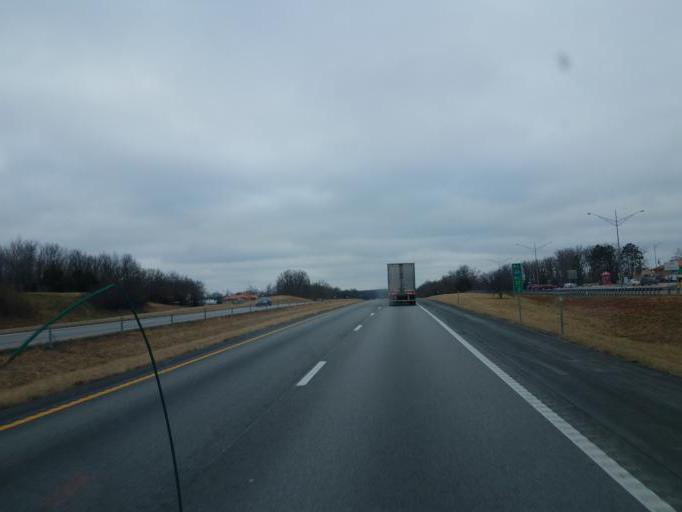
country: US
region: Missouri
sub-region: Webster County
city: Marshfield
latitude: 37.4764
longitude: -92.8561
